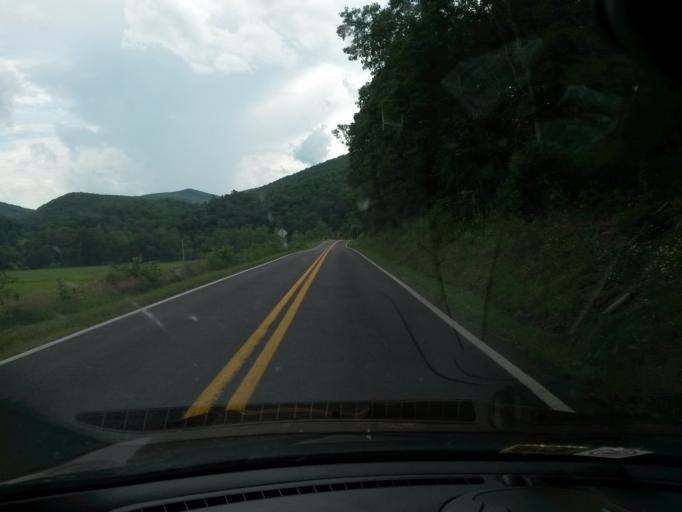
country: US
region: West Virginia
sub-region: Pendleton County
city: Franklin
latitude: 38.6028
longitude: -79.3645
